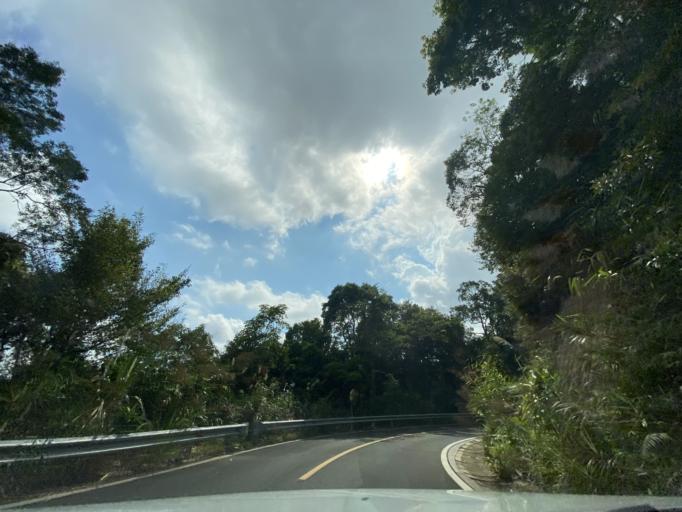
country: CN
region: Hainan
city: Benhao
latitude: 18.6981
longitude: 109.8824
